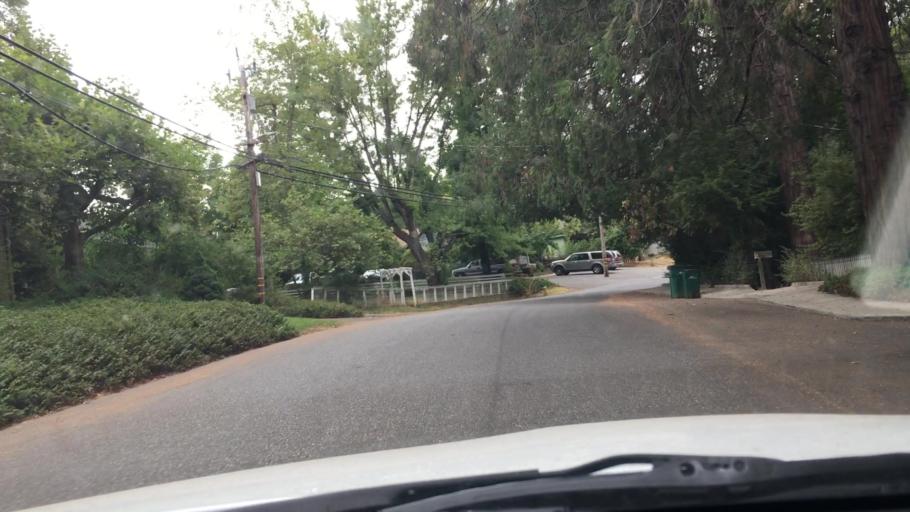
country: US
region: California
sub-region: Nevada County
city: Nevada City
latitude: 39.2590
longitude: -121.0228
